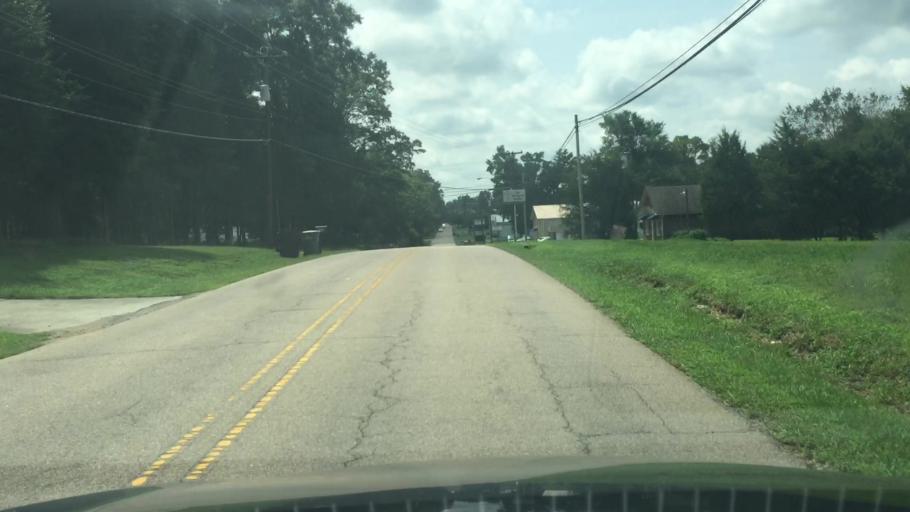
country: US
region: North Carolina
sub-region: Cabarrus County
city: Kannapolis
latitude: 35.4727
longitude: -80.6221
